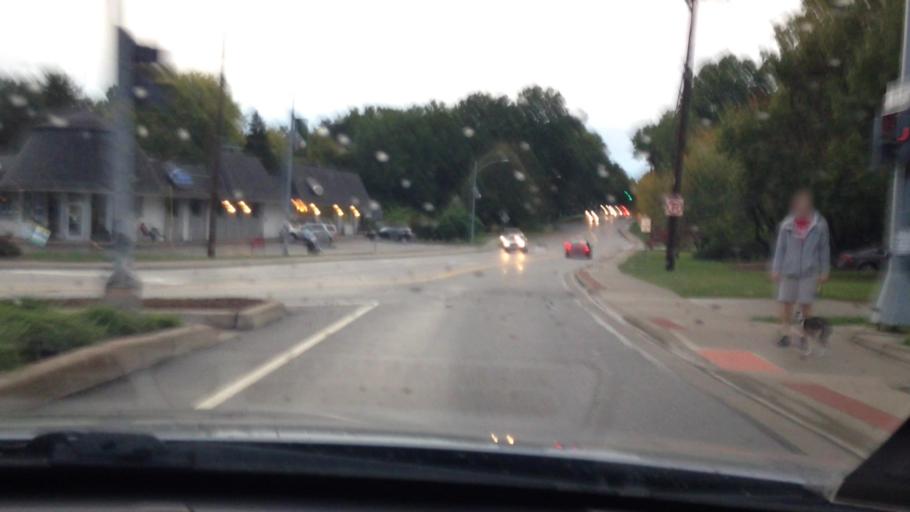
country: US
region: Kansas
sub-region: Johnson County
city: Leawood
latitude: 38.9843
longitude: -94.6126
